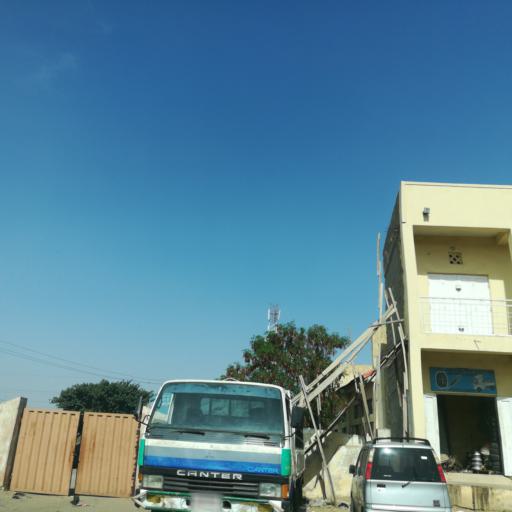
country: NG
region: Kano
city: Kano
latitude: 12.0105
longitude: 8.5228
